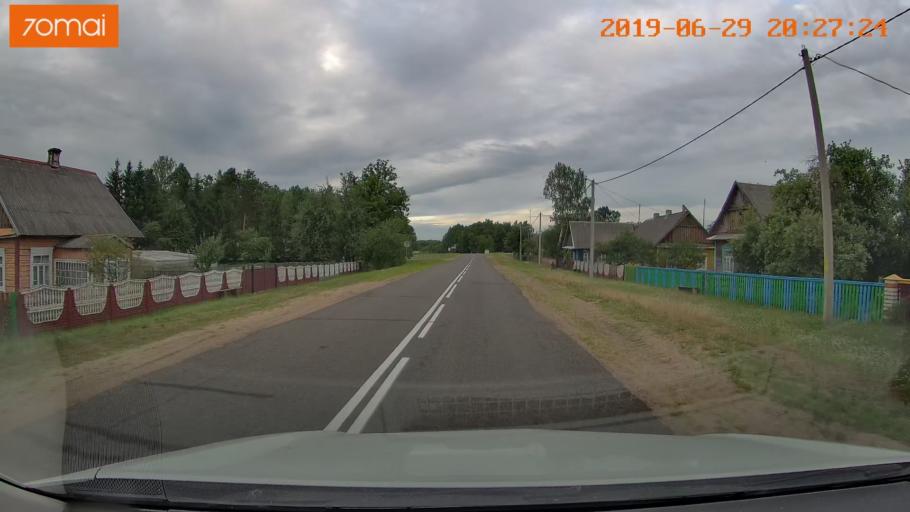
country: BY
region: Brest
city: Hantsavichy
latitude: 52.4734
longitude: 26.3041
